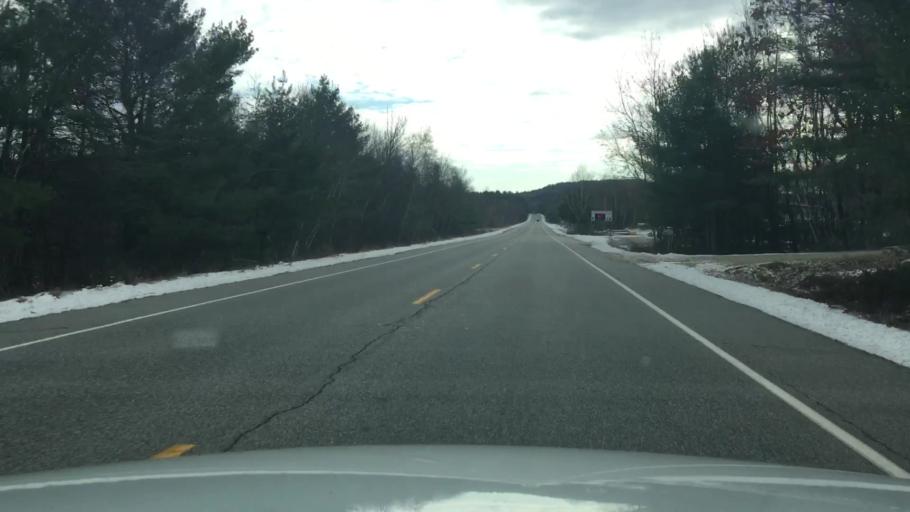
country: US
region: Maine
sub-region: Oxford County
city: Canton
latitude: 44.4303
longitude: -70.3013
